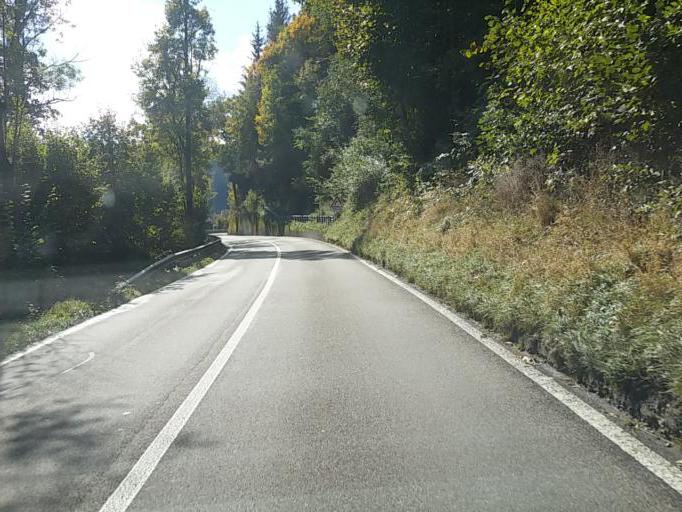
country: CH
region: Bern
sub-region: Emmental District
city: Trachselwald
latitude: 47.0151
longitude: 7.7238
